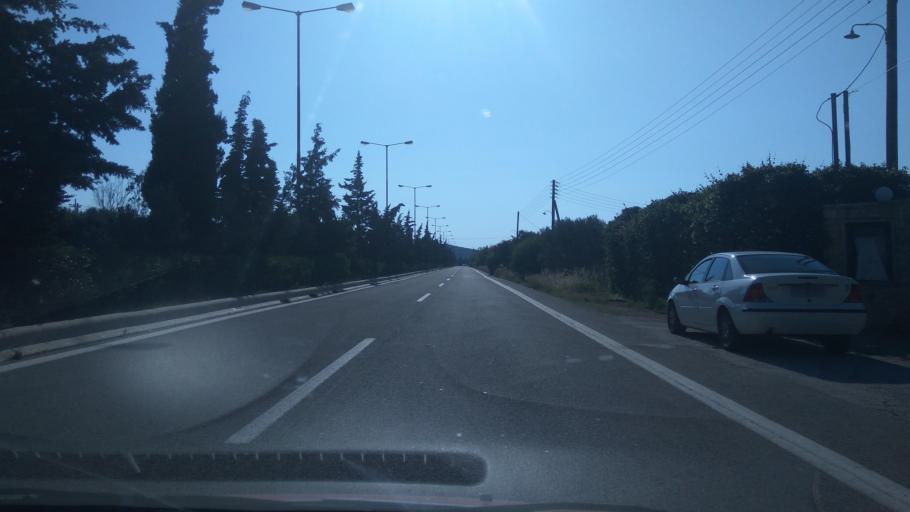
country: GR
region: Attica
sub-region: Nomarchia Anatolikis Attikis
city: Keratea
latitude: 37.8028
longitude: 24.0284
